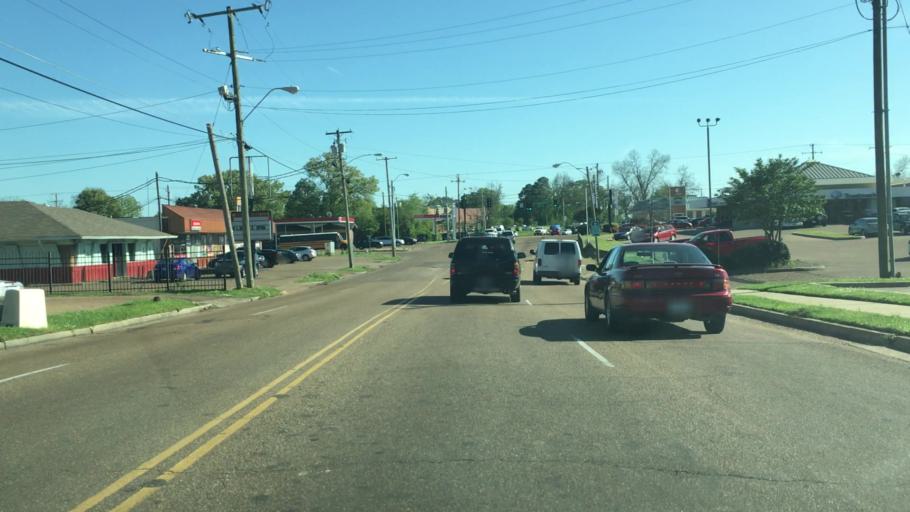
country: US
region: Mississippi
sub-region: Hinds County
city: Jackson
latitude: 32.3282
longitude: -90.1927
